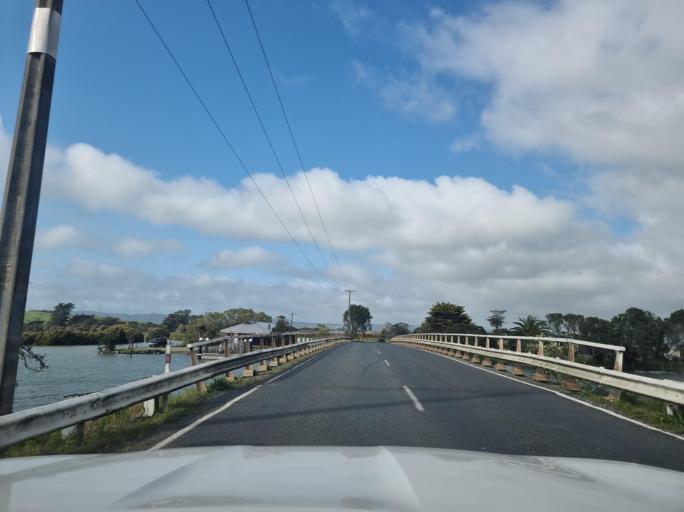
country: NZ
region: Northland
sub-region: Whangarei
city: Ruakaka
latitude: -35.9766
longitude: 174.4538
